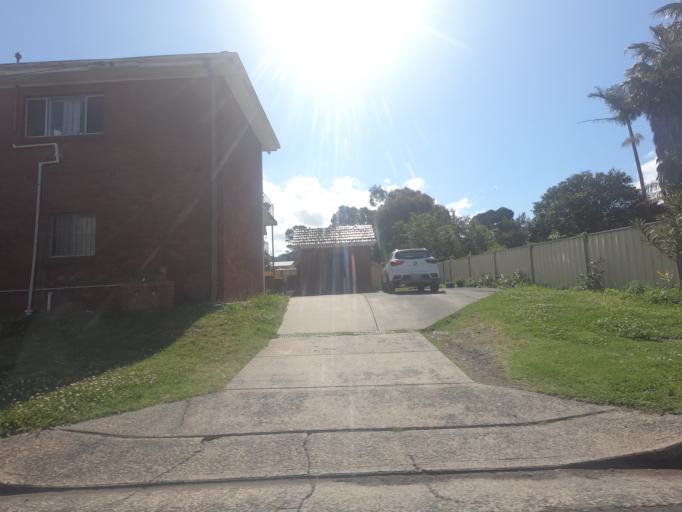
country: AU
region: New South Wales
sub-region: Wollongong
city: Cordeaux Heights
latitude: -34.4546
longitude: 150.8340
